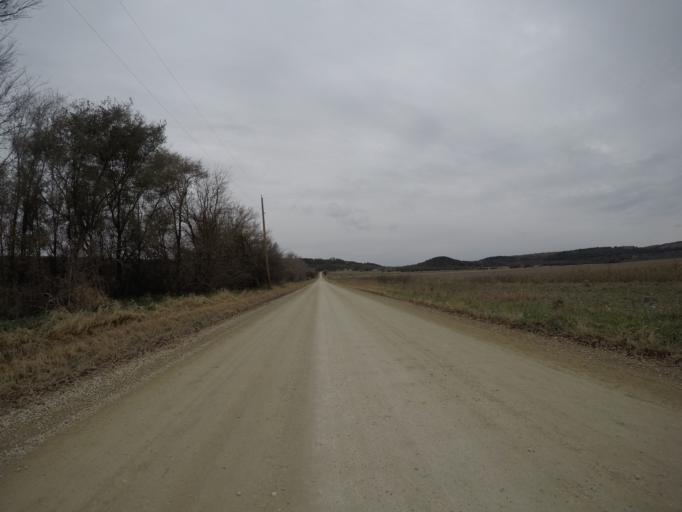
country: US
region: Kansas
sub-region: Riley County
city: Ogden
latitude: 39.1626
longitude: -96.6819
